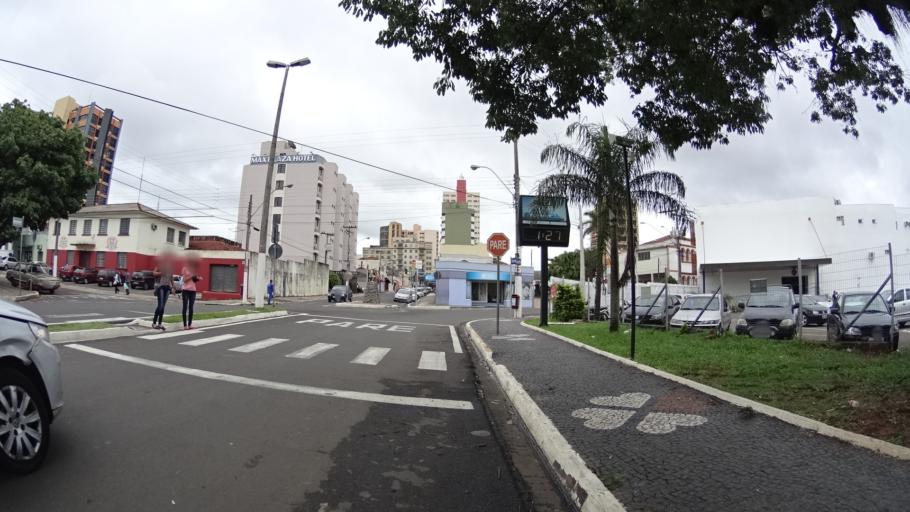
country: BR
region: Sao Paulo
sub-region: Marilia
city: Marilia
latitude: -22.2181
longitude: -49.9460
